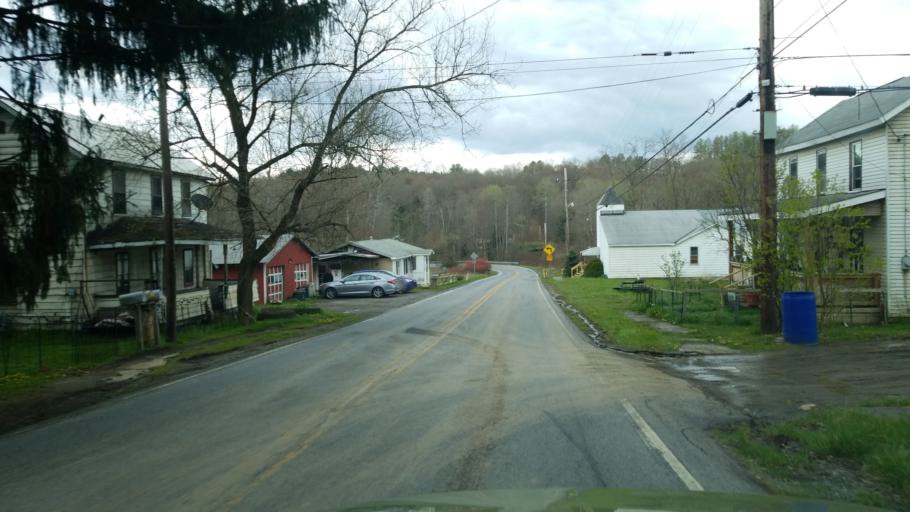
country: US
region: Pennsylvania
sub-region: Clearfield County
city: Curwensville
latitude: 40.8899
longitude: -78.4600
